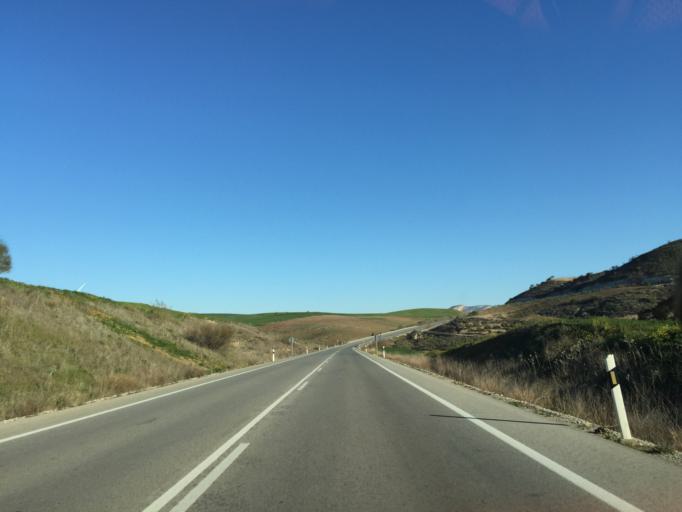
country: ES
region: Andalusia
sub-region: Provincia de Malaga
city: Ardales
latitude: 36.9054
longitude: -4.8409
